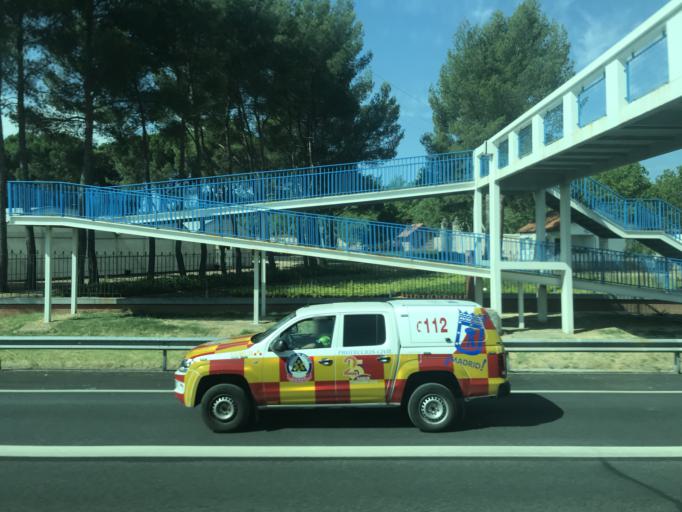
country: ES
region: Madrid
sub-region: Provincia de Madrid
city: Moncloa-Aravaca
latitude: 40.4253
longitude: -3.7320
